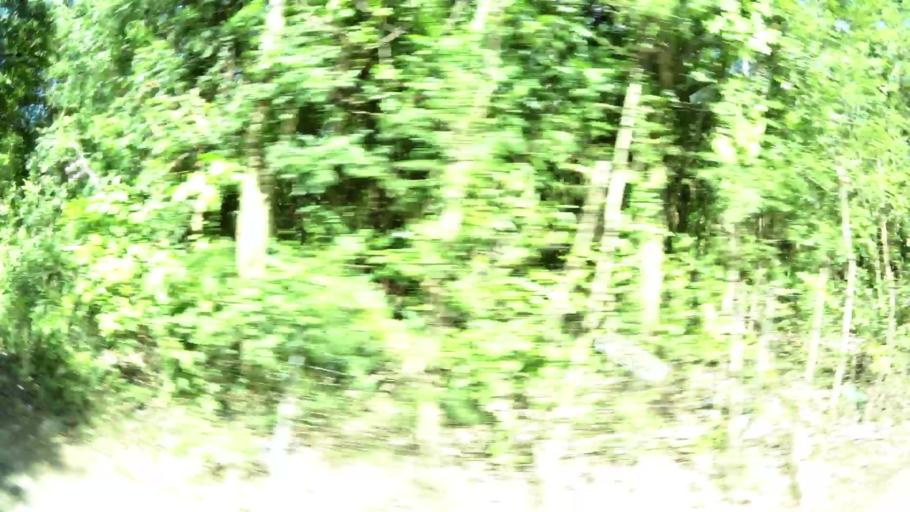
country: GP
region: Guadeloupe
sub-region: Guadeloupe
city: Saint-Francois
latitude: 16.2532
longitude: -61.2813
